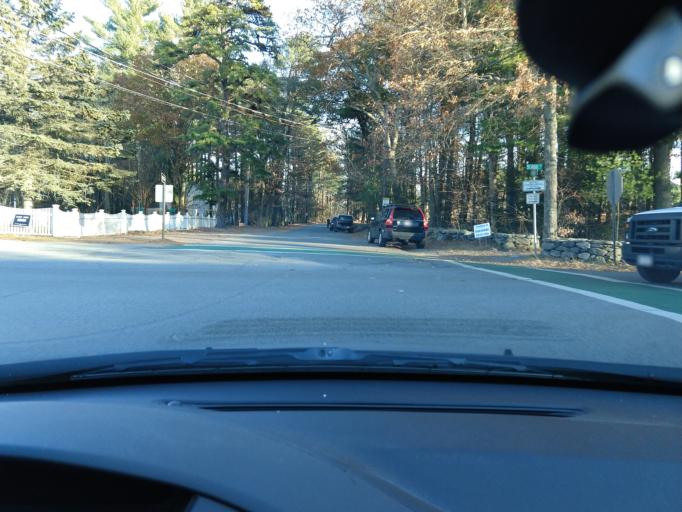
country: US
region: Massachusetts
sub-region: Middlesex County
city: Carlisle
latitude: 42.5279
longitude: -71.3499
